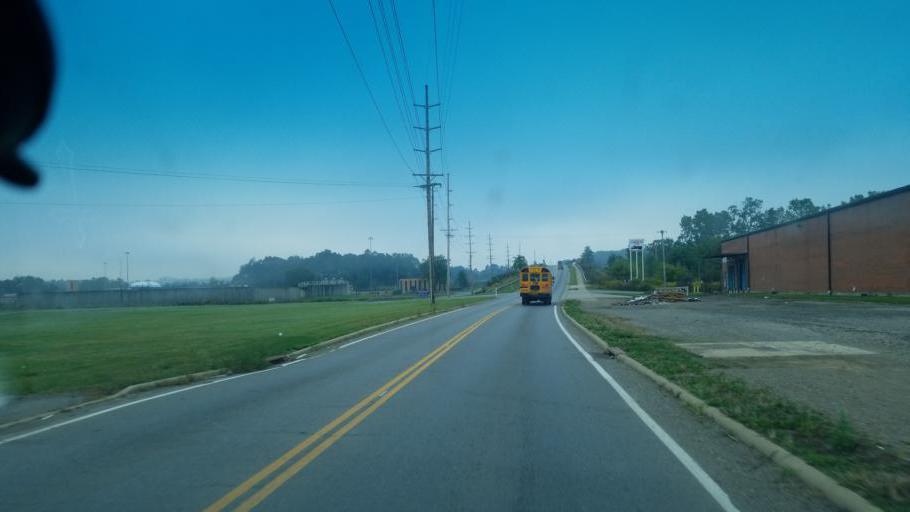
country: US
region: Ohio
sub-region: Richland County
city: Lincoln Heights
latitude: 40.7508
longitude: -82.4844
